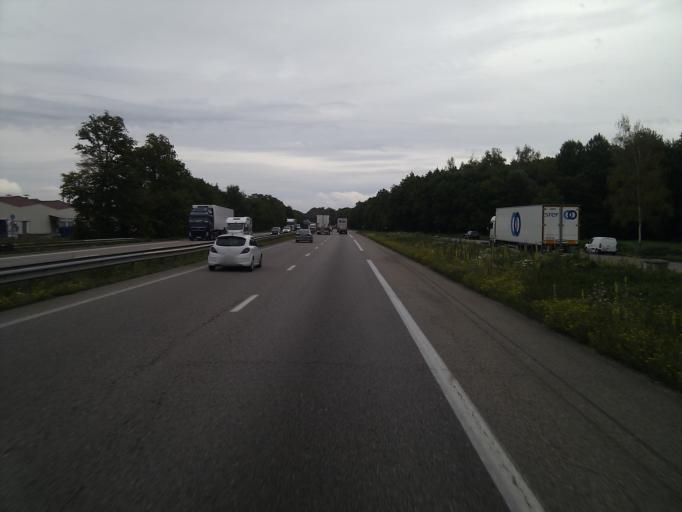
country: FR
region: Lorraine
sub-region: Departement de Meurthe-et-Moselle
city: Velaine-en-Haye
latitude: 48.6884
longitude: 6.0103
